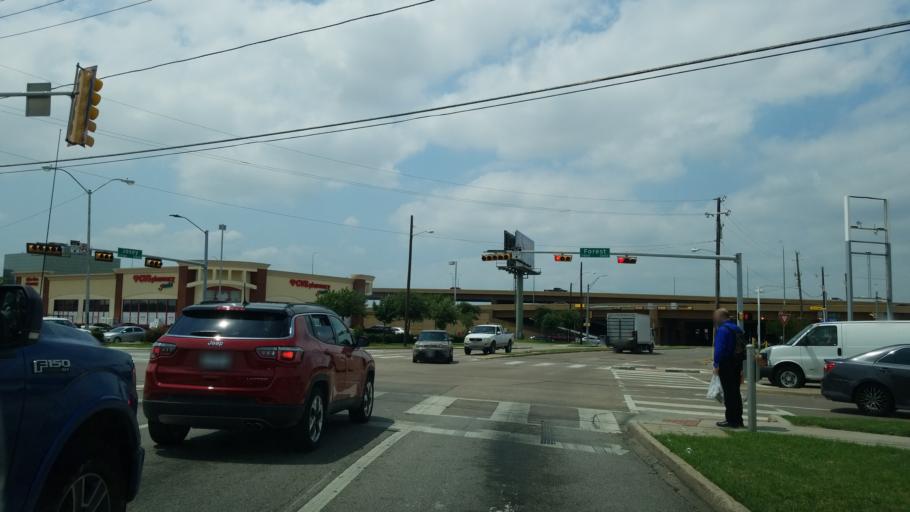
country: US
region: Texas
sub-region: Dallas County
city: Farmers Branch
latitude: 32.9092
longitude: -96.8815
